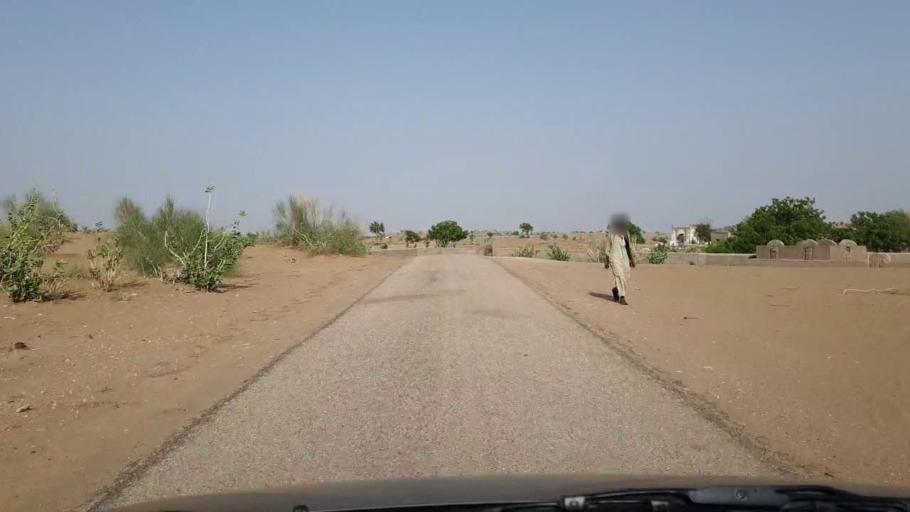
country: PK
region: Sindh
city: Chor
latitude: 25.4529
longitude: 70.5274
